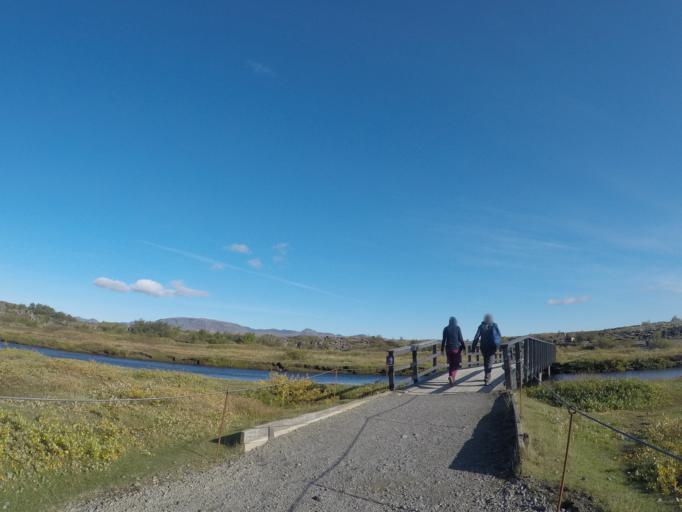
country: IS
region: South
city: Hveragerdi
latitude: 64.2592
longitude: -21.1197
